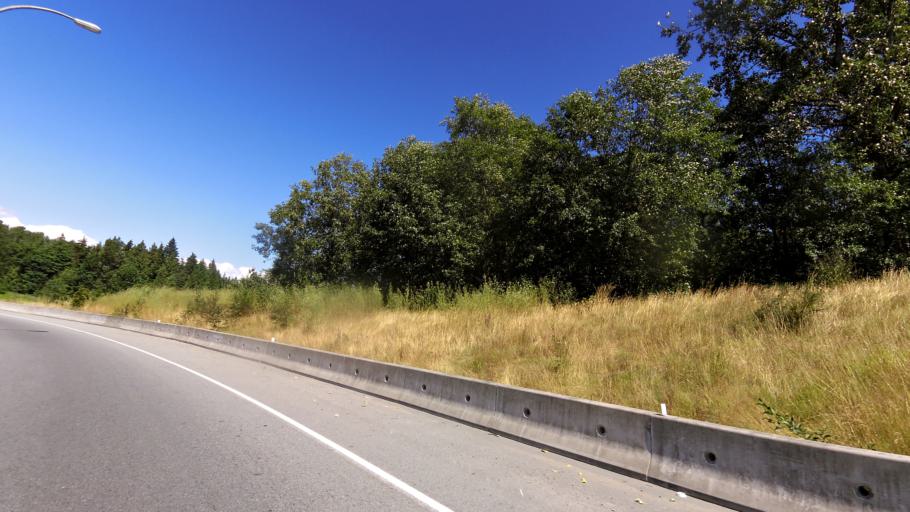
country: CA
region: British Columbia
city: New Westminster
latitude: 49.2409
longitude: -122.9145
